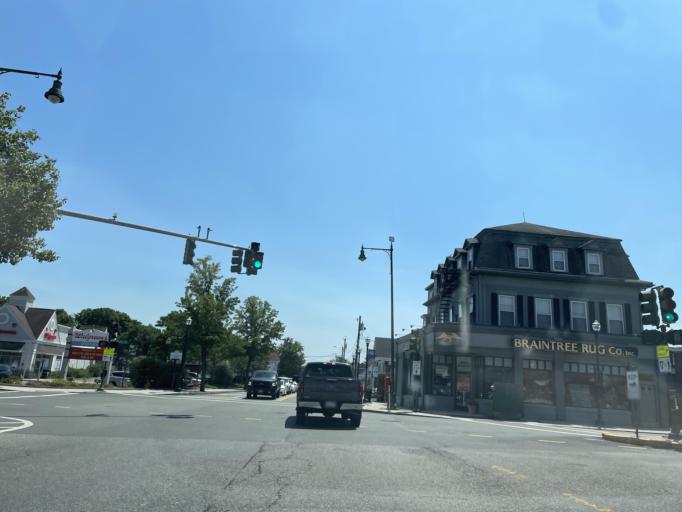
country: US
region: Massachusetts
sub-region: Norfolk County
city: Braintree
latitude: 42.2025
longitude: -71.0051
